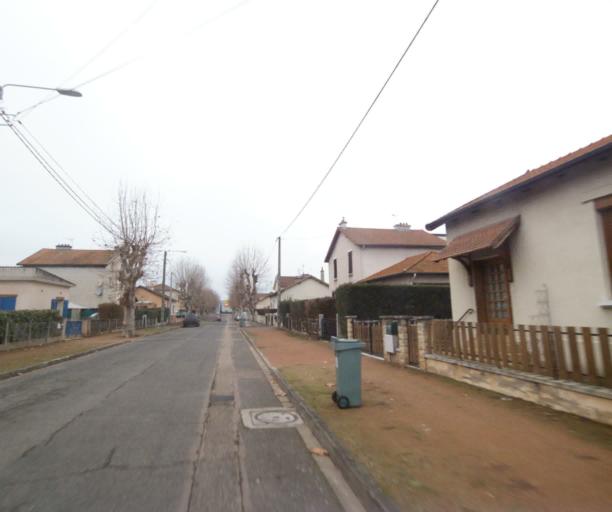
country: FR
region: Rhone-Alpes
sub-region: Departement de la Loire
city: Le Coteau
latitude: 46.0544
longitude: 4.0887
